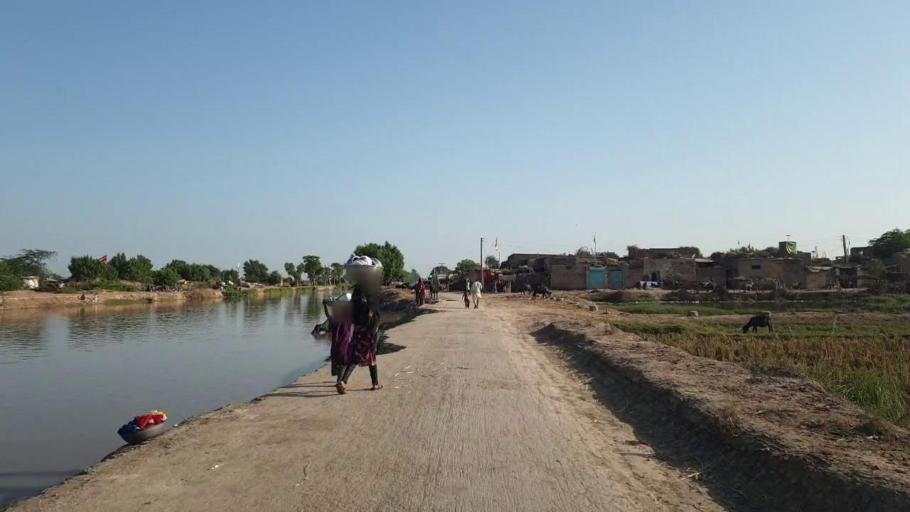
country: PK
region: Sindh
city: Hyderabad
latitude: 25.3244
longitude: 68.4263
